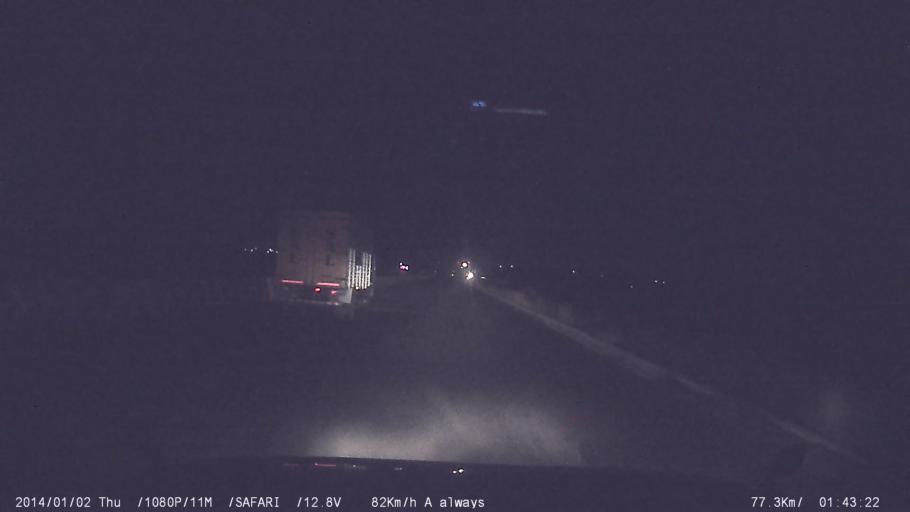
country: IN
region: Tamil Nadu
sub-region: Tiruppur
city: Avinashi
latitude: 11.1766
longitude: 77.2426
